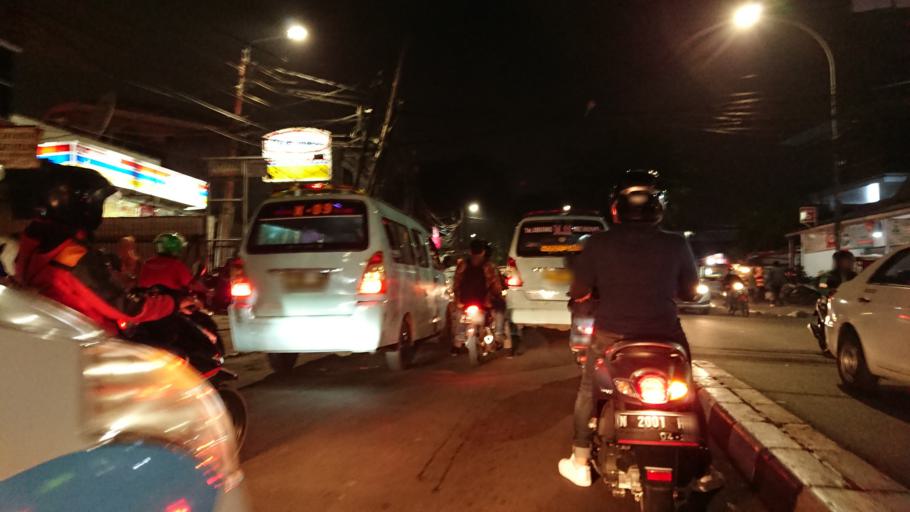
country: ID
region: Jakarta Raya
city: Jakarta
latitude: -6.2022
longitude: 106.7987
